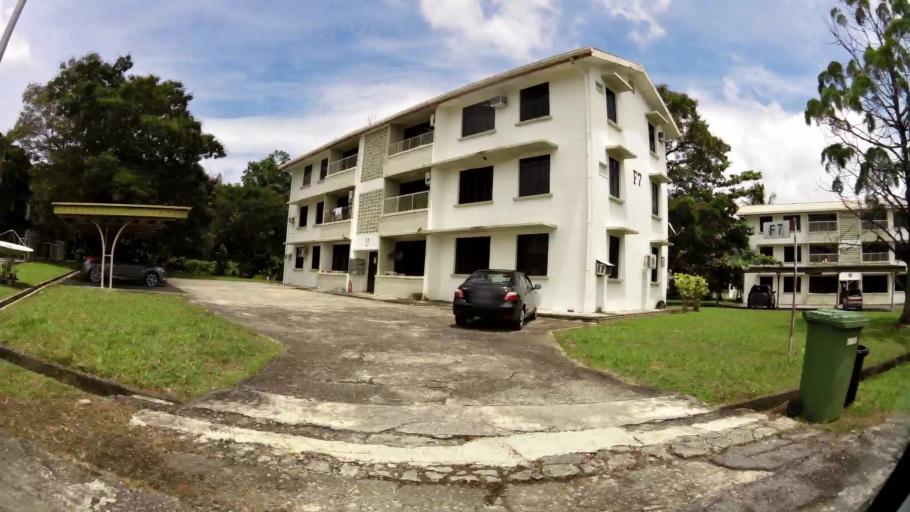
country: BN
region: Brunei and Muara
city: Bandar Seri Begawan
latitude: 4.9188
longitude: 114.9324
